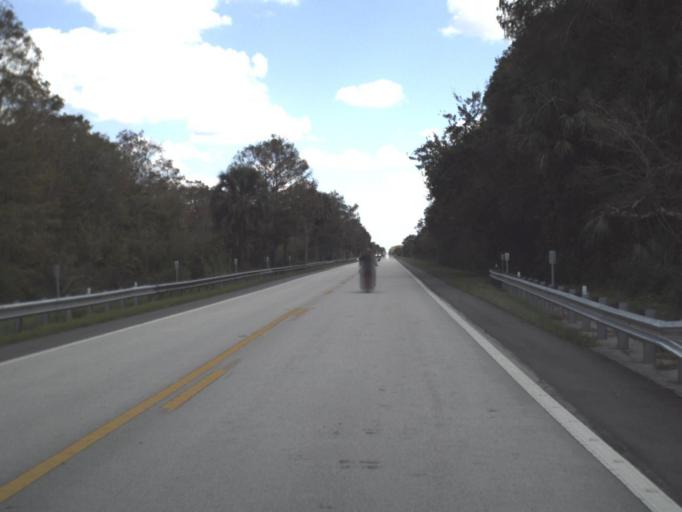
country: US
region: Florida
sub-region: Collier County
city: Marco
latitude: 25.8767
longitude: -81.2283
